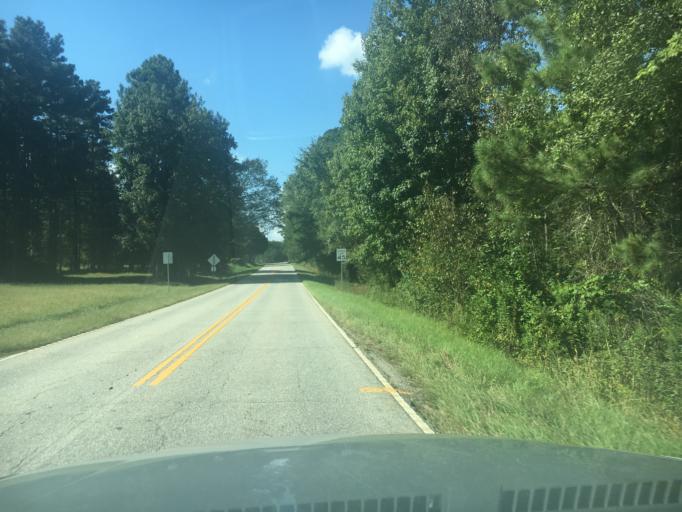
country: US
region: South Carolina
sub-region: Greenwood County
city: Greenwood
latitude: 34.2744
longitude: -82.1950
